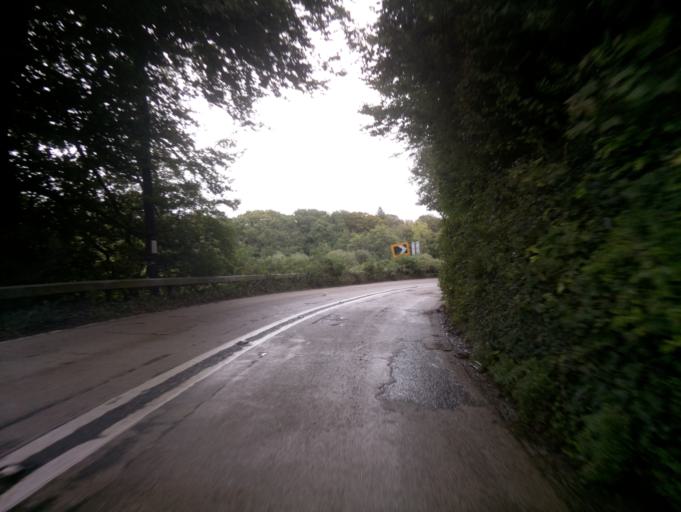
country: GB
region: England
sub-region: Devon
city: Modbury
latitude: 50.3397
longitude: -3.8599
